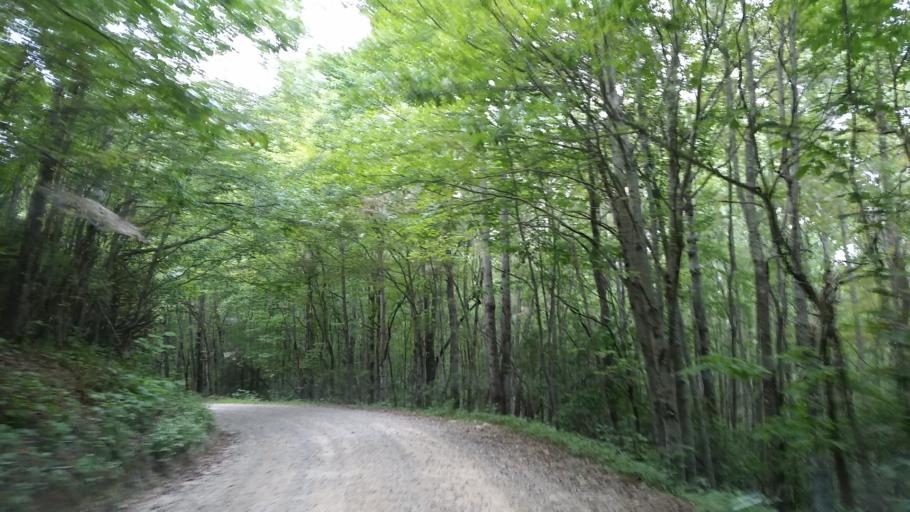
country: US
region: Georgia
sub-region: Lumpkin County
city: Dahlonega
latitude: 34.6457
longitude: -84.0579
